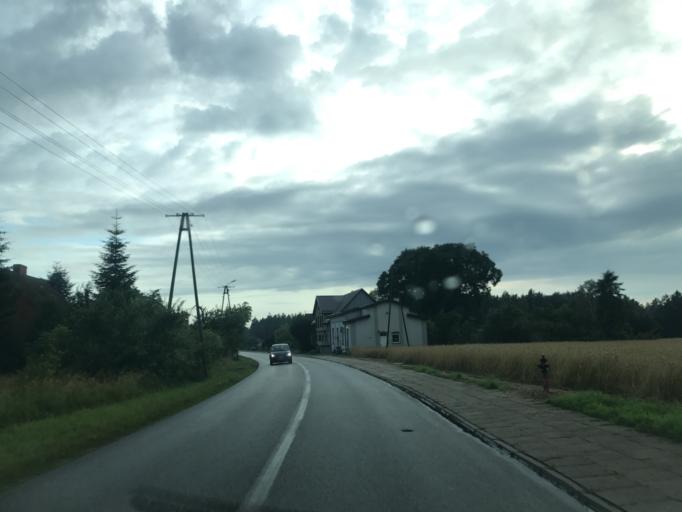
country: PL
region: West Pomeranian Voivodeship
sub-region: Powiat bialogardzki
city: Tychowo
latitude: 53.9492
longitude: 16.3412
